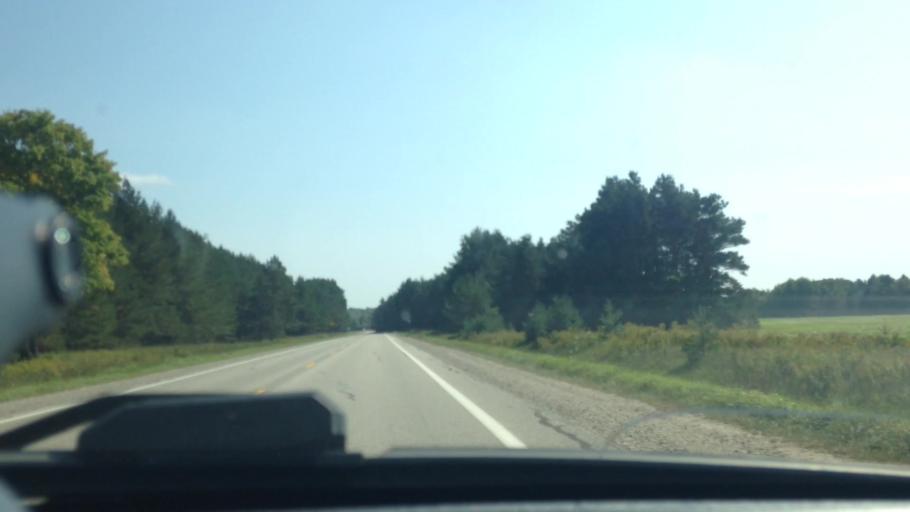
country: US
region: Michigan
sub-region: Luce County
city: Newberry
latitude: 46.3169
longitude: -85.6645
